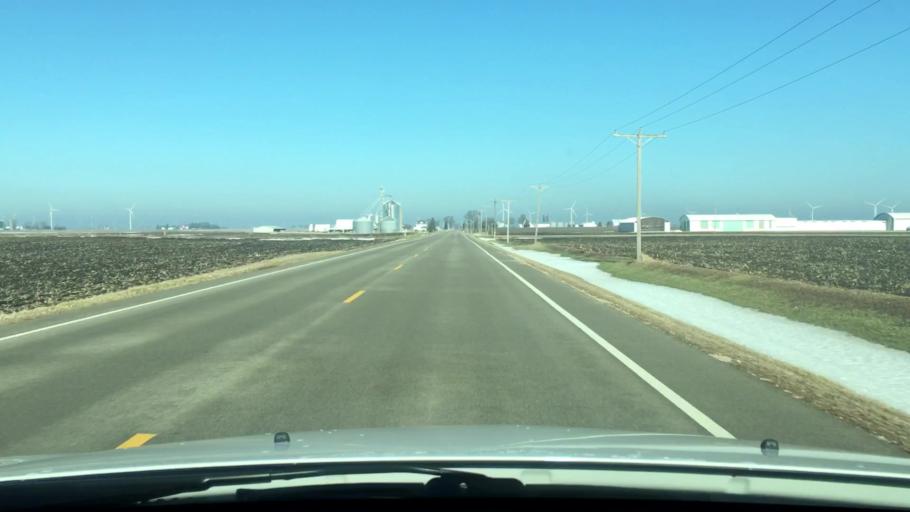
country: US
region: Illinois
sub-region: DeKalb County
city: Waterman
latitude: 41.7810
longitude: -88.8772
